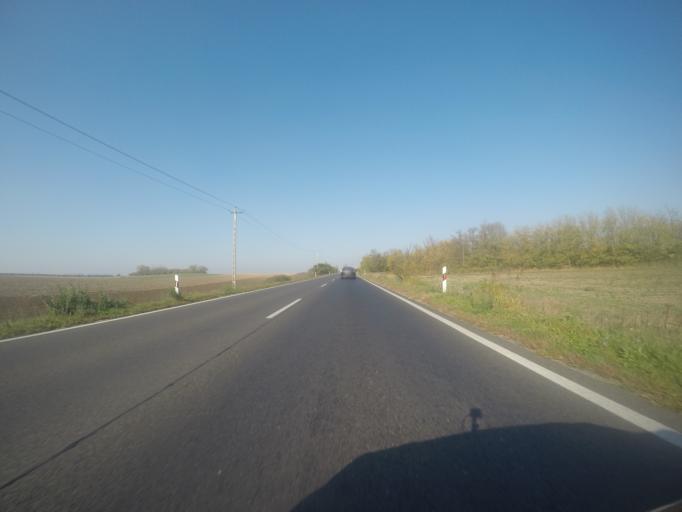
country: HU
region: Fejer
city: Baracs
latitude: 46.8564
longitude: 18.9132
